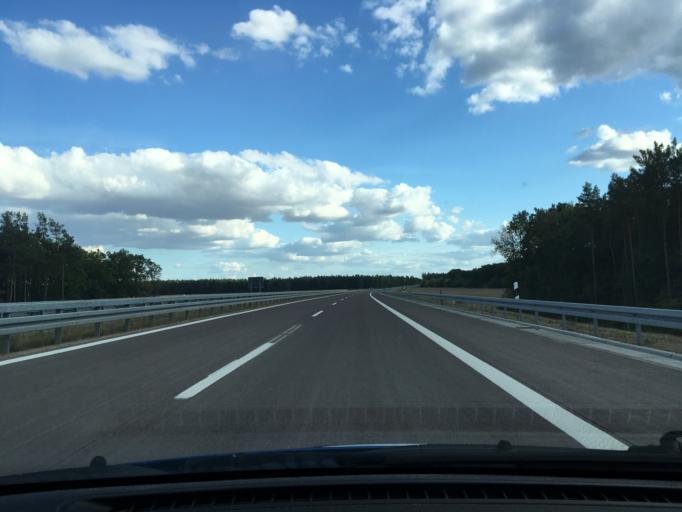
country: DE
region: Mecklenburg-Vorpommern
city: Gross Laasch
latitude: 53.3357
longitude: 11.5241
